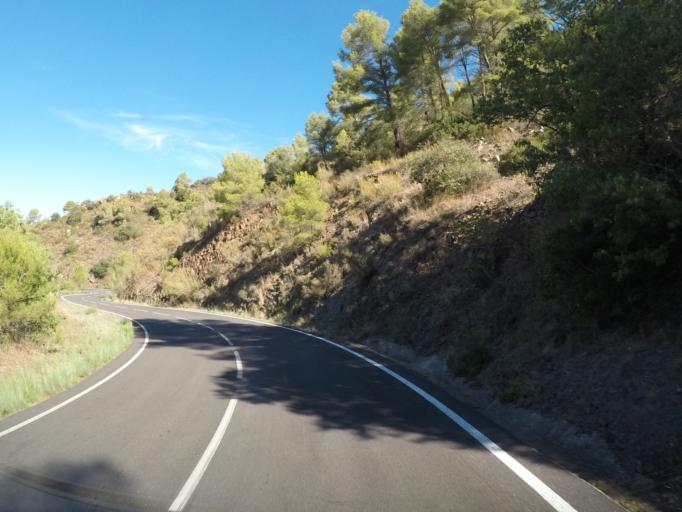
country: ES
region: Catalonia
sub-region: Provincia de Tarragona
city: Falset
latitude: 41.1725
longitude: 0.7987
